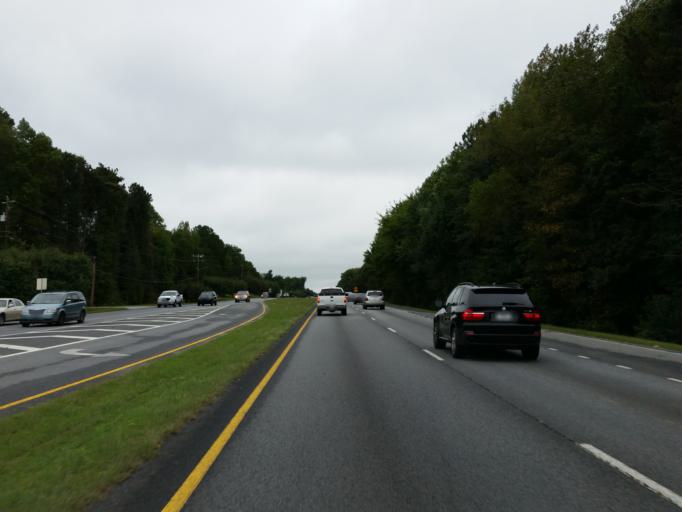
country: US
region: Georgia
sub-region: Clayton County
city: Jonesboro
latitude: 33.5049
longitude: -84.3526
